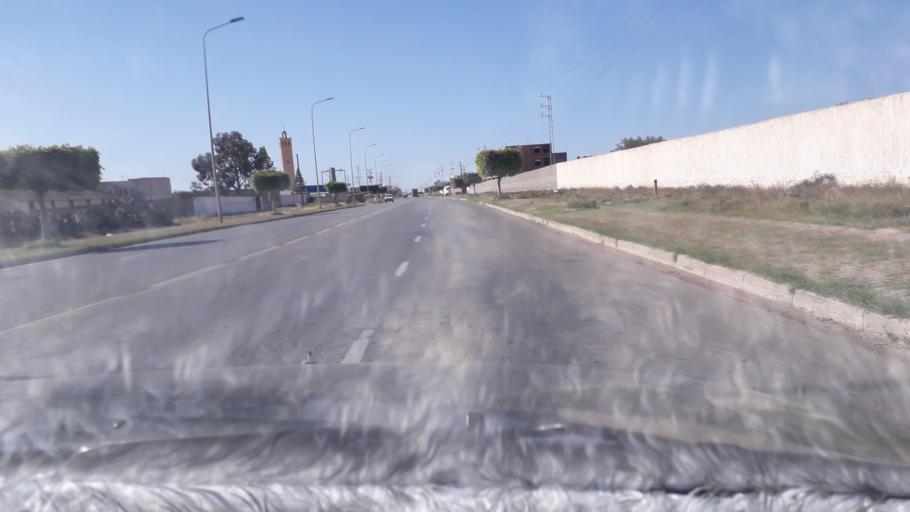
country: TN
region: Safaqis
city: Al Qarmadah
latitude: 34.8521
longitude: 10.7610
